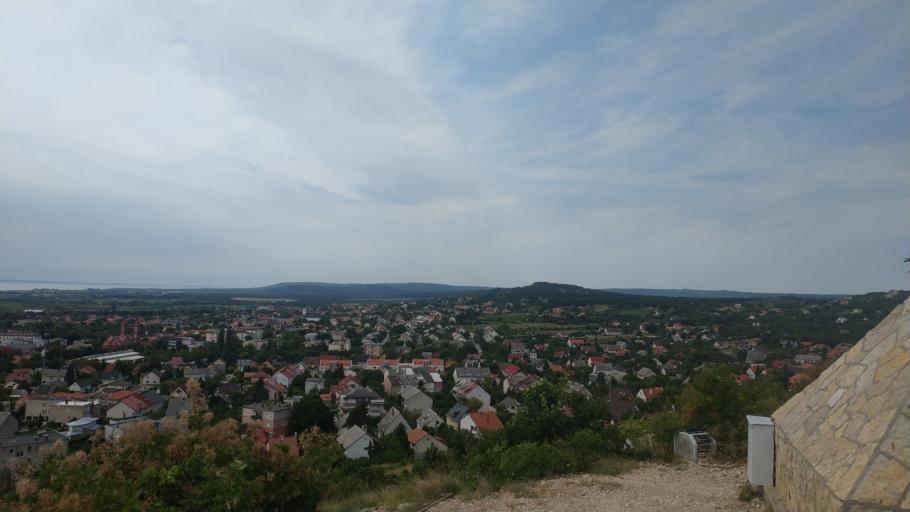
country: HU
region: Veszprem
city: Balatonfured
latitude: 46.9673
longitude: 17.8818
